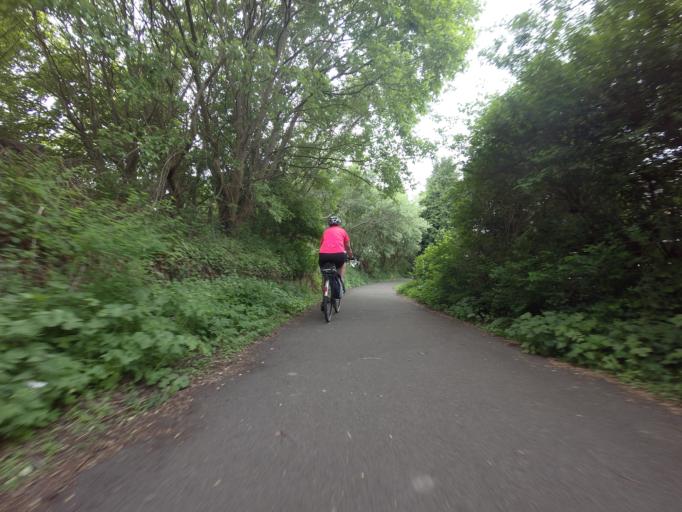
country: GB
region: Scotland
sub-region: Fife
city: Townhill
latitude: 56.0868
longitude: -3.4420
